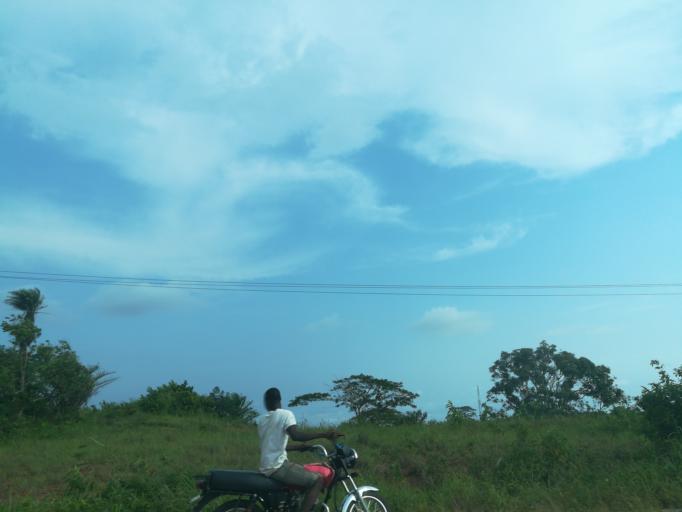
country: NG
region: Lagos
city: Ikorodu
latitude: 6.6219
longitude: 3.6593
